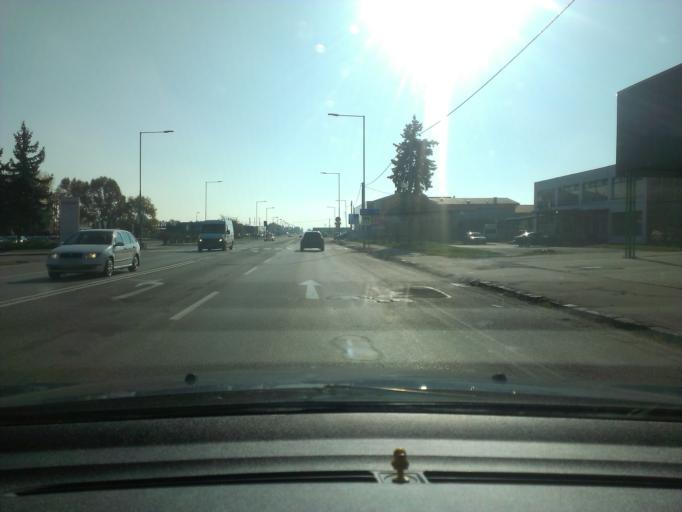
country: SK
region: Nitriansky
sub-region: Okres Nove Zamky
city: Nove Zamky
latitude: 47.9778
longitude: 18.1783
